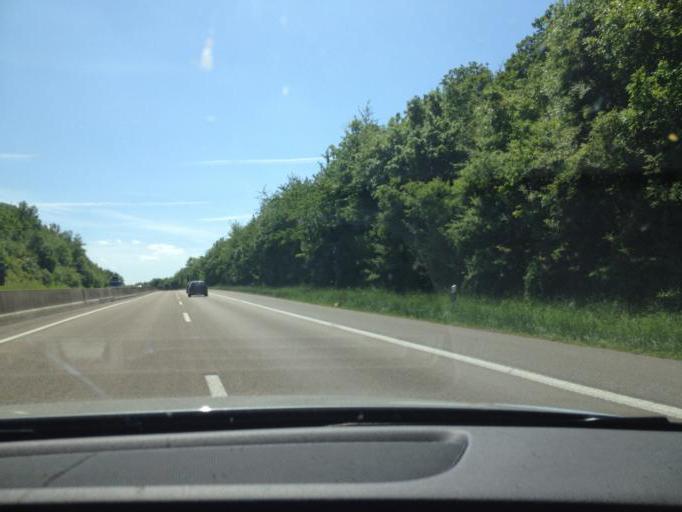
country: DE
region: North Rhine-Westphalia
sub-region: Regierungsbezirk Koln
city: Euskirchen
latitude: 50.6360
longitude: 6.7197
